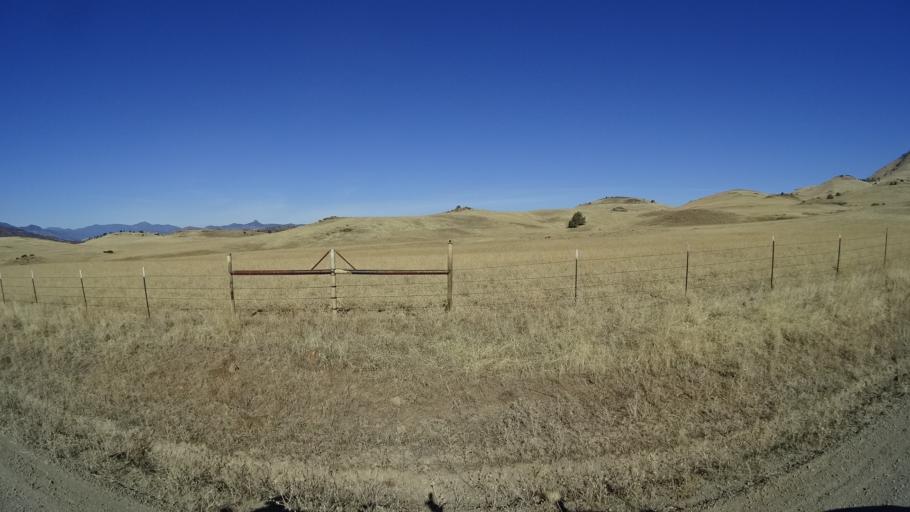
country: US
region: California
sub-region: Siskiyou County
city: Montague
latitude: 41.8468
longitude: -122.4370
